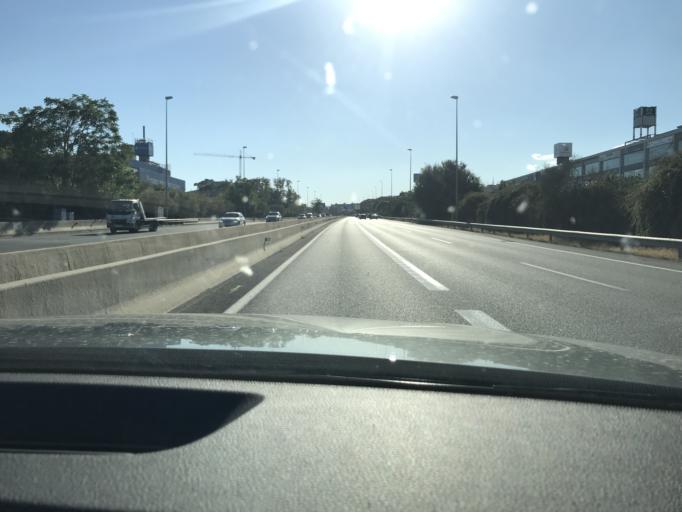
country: ES
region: Catalonia
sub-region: Provincia de Barcelona
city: Badalona
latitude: 41.4593
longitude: 2.2562
